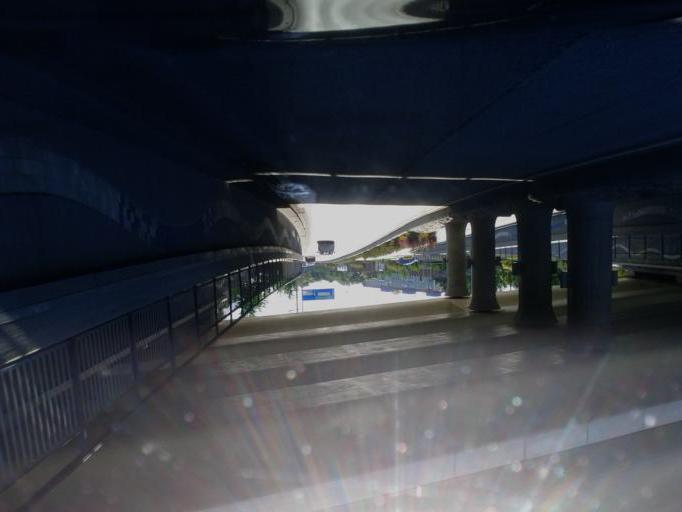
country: SE
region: Stockholm
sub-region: Taby Kommun
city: Taby
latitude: 59.4479
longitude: 18.0929
